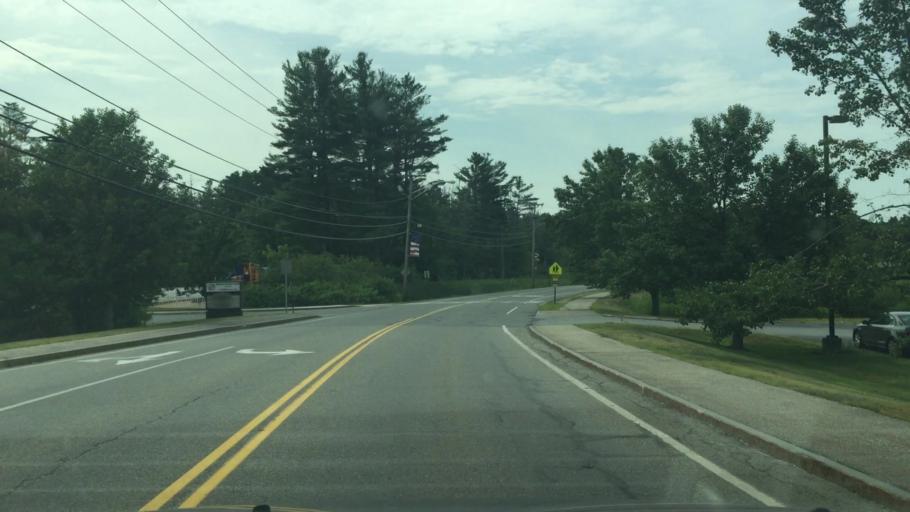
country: US
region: New Hampshire
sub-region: Rockingham County
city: Salem
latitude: 42.7847
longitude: -71.2104
